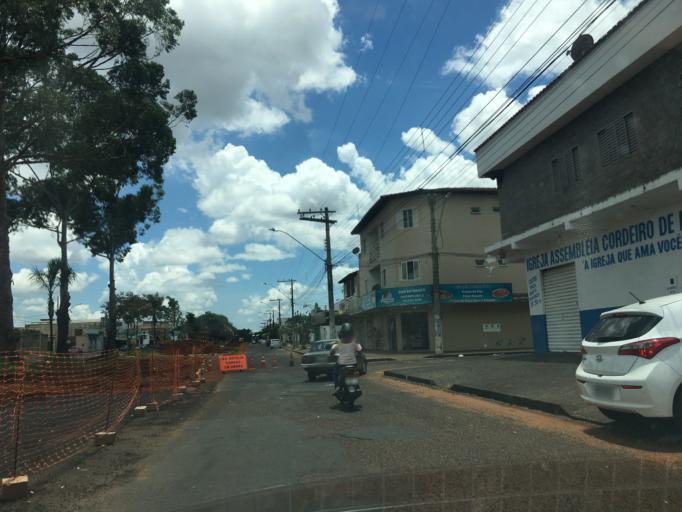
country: BR
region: Minas Gerais
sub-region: Uberlandia
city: Uberlandia
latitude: -18.9476
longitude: -48.3128
